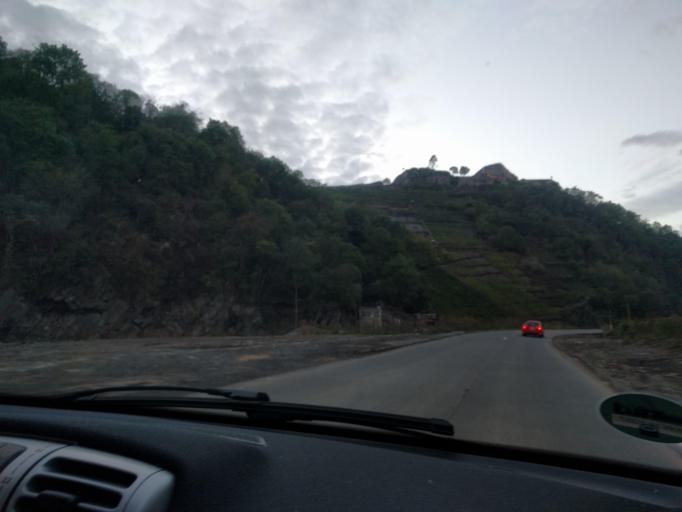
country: DE
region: Rheinland-Pfalz
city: Rech
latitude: 50.5174
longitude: 7.0283
